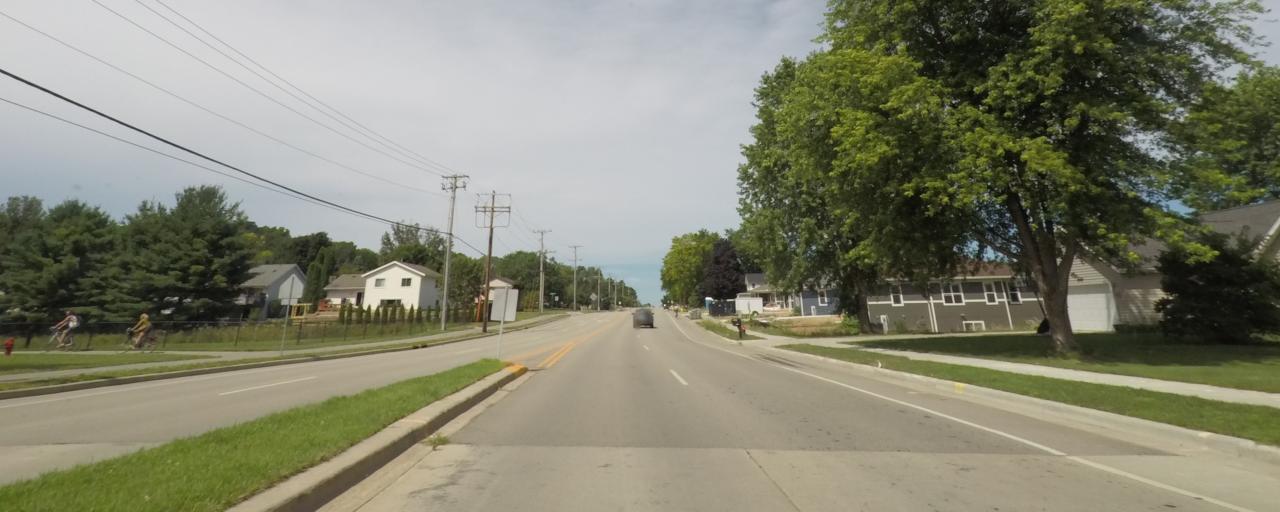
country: US
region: Wisconsin
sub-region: Dane County
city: McFarland
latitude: 43.0260
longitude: -89.2864
